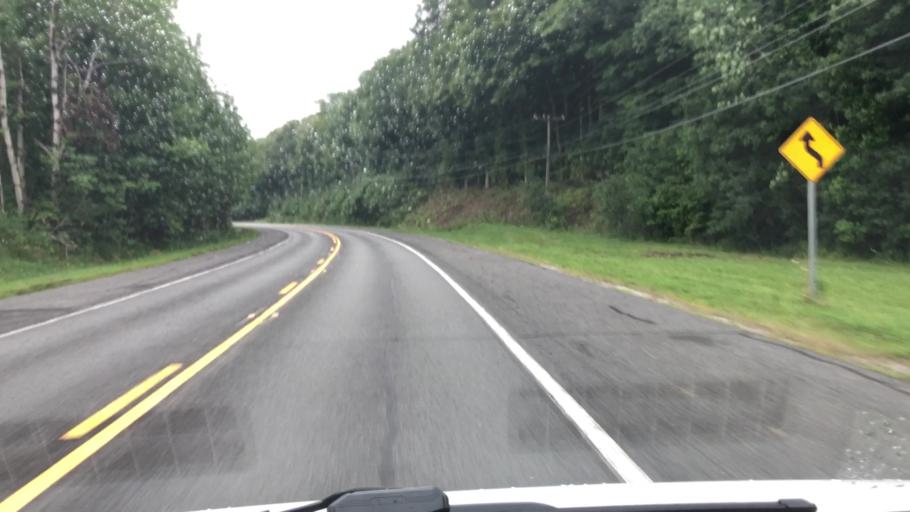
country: US
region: Massachusetts
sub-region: Berkshire County
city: Lanesborough
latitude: 42.5851
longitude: -73.2513
